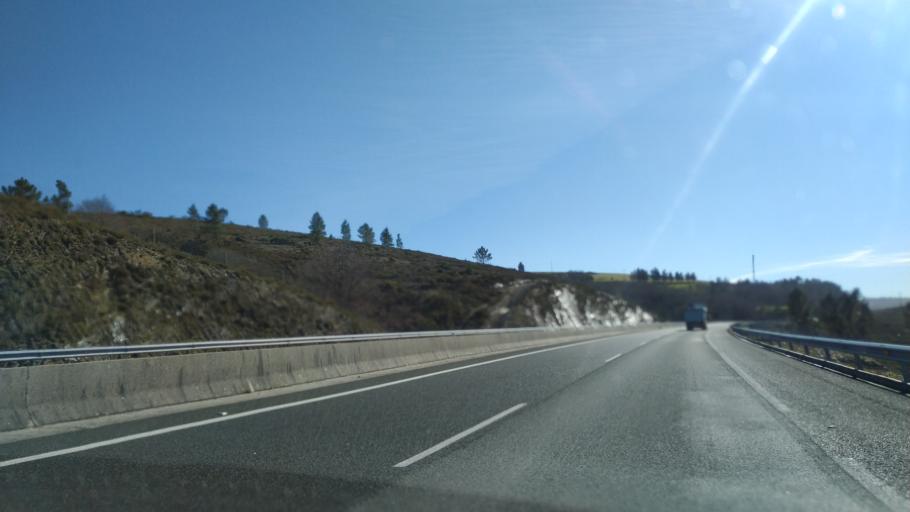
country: ES
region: Galicia
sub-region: Provincia de Pontevedra
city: Lalin
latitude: 42.5982
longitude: -8.0893
